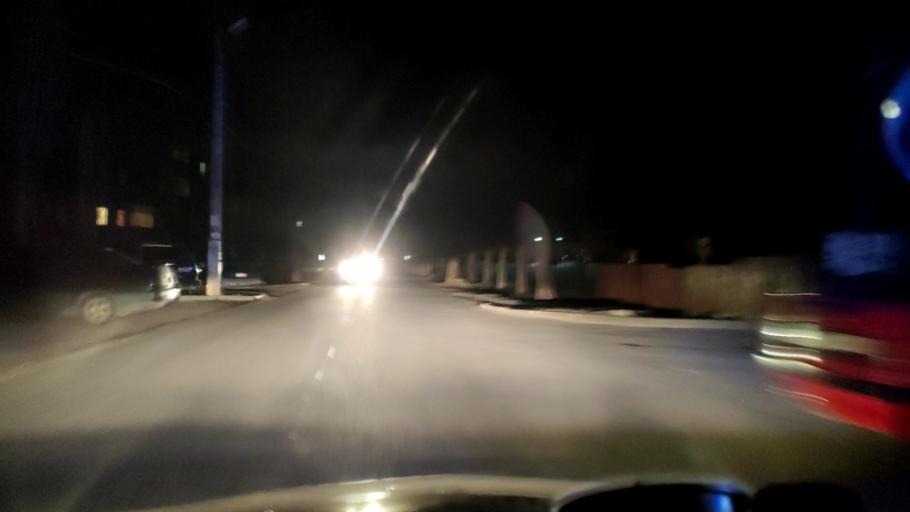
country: RU
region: Voronezj
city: Semiluki
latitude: 51.6931
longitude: 39.0167
